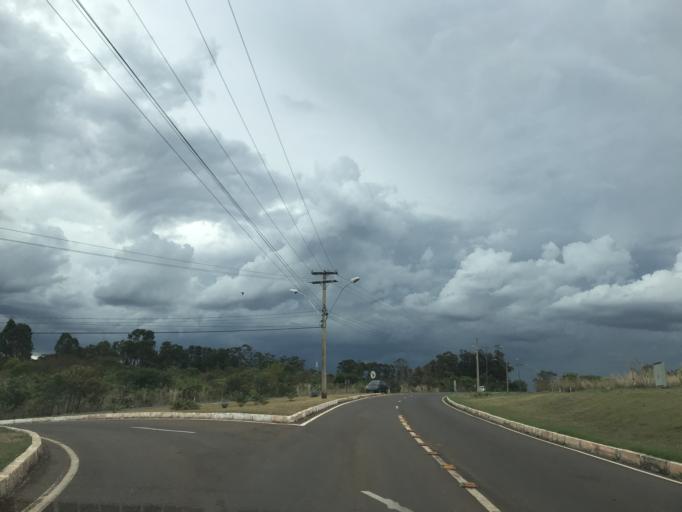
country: BR
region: Federal District
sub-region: Brasilia
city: Brasilia
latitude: -15.9012
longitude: -47.9156
